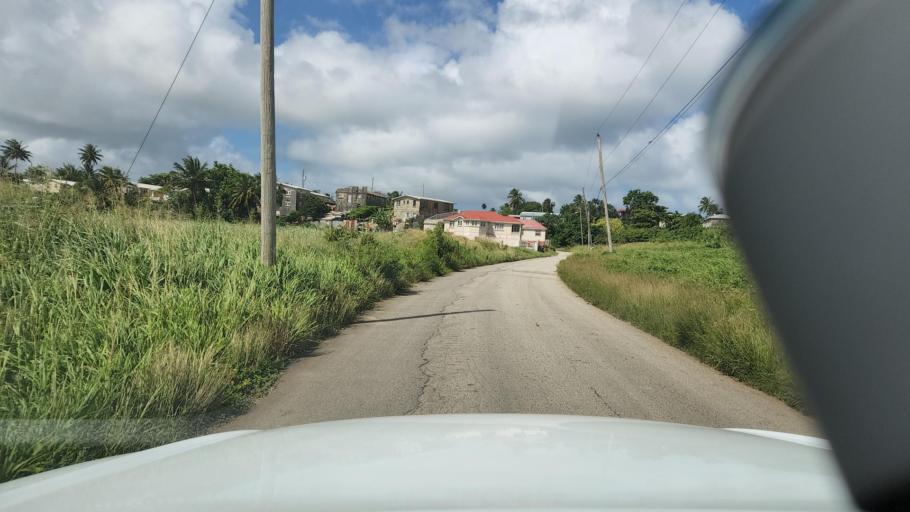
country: BB
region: Saint John
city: Four Cross Roads
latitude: 13.1915
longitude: -59.5093
